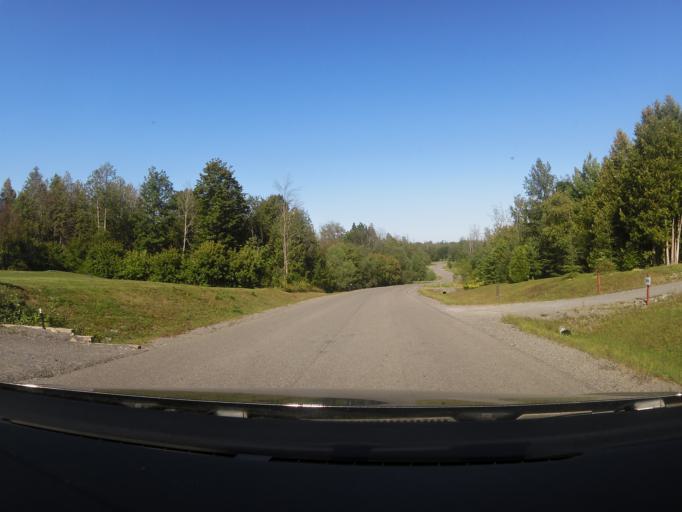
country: CA
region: Ontario
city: Carleton Place
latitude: 45.3051
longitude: -76.0772
